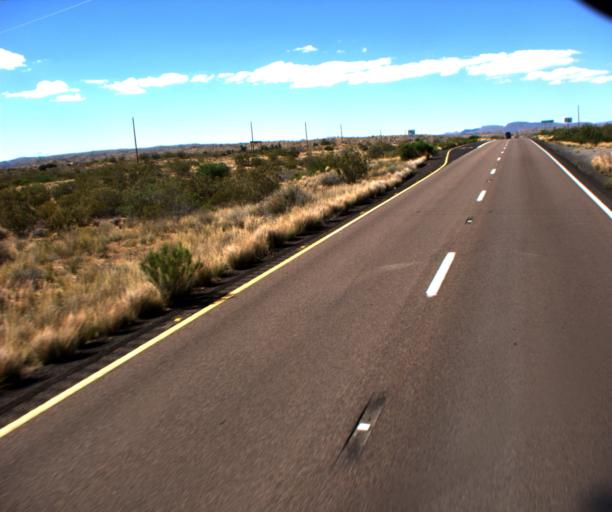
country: US
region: Arizona
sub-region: Mohave County
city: Kingman
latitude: 35.0266
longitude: -113.6642
